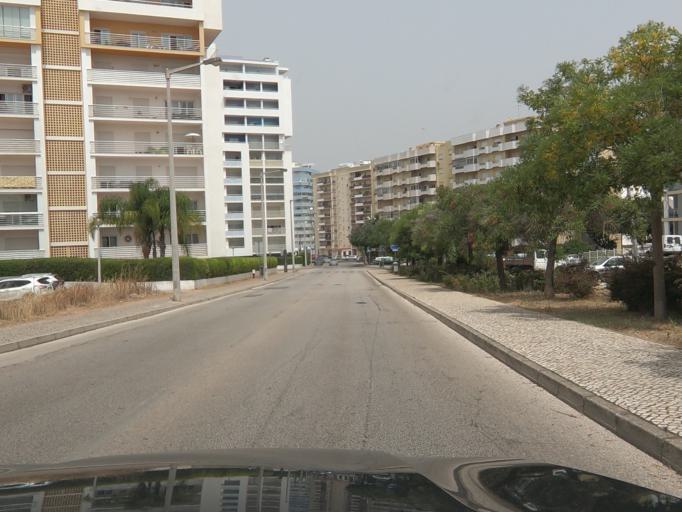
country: PT
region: Faro
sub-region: Portimao
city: Portimao
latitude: 37.1299
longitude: -8.5429
